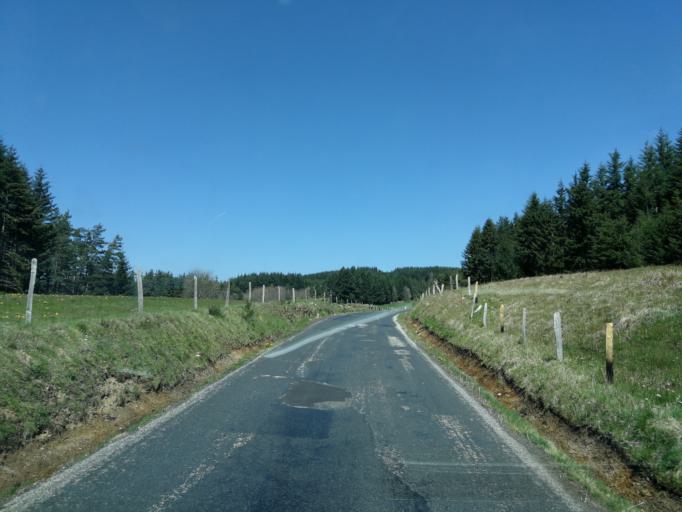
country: FR
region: Rhone-Alpes
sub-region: Departement de l'Ardeche
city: Le Cheylard
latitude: 44.9451
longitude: 4.4194
